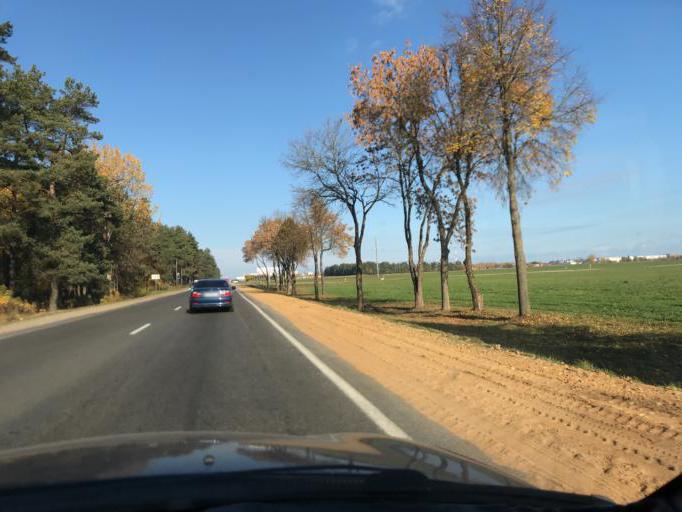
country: BY
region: Grodnenskaya
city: Lida
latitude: 53.8755
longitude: 25.2586
